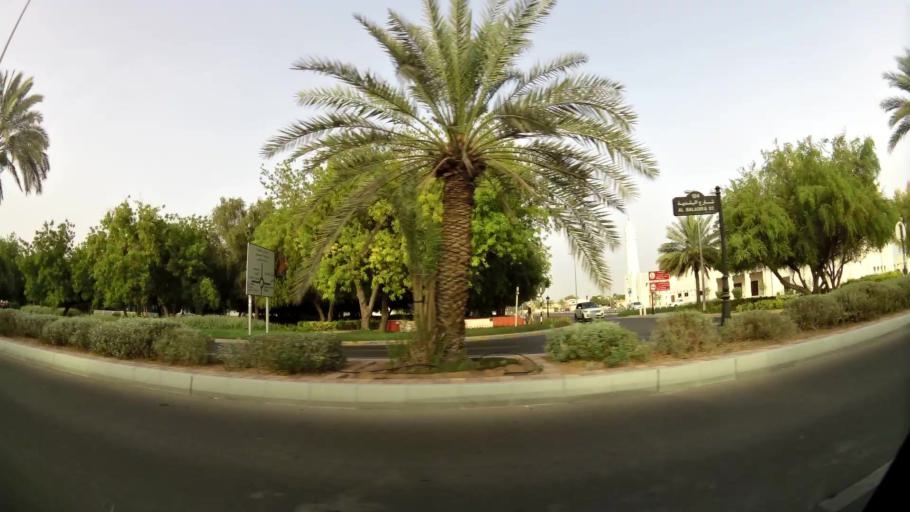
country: OM
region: Al Buraimi
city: Al Buraymi
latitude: 24.2457
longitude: 55.7393
